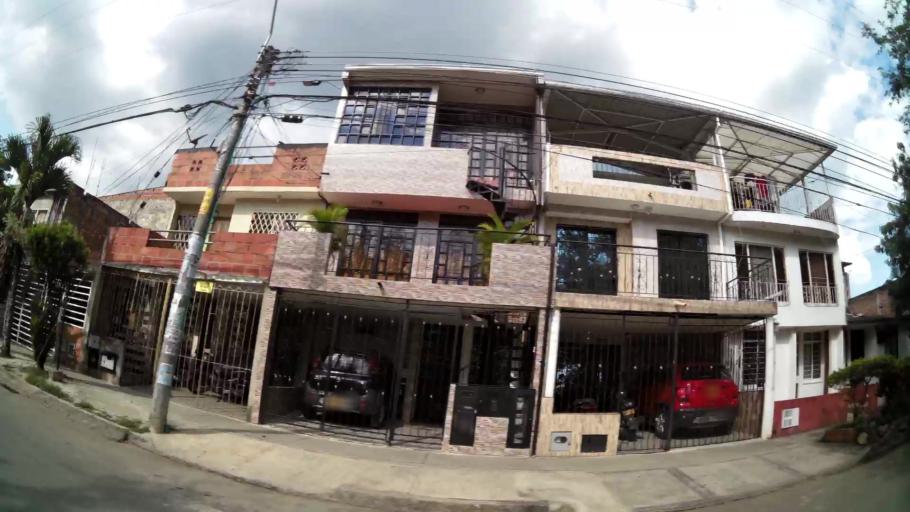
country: CO
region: Valle del Cauca
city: Cali
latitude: 3.3965
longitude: -76.5058
